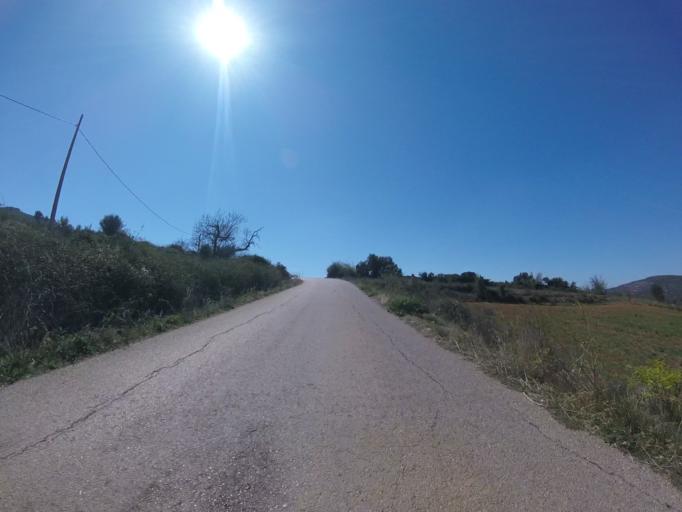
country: ES
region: Valencia
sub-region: Provincia de Castello
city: Chert/Xert
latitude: 40.4109
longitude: 0.1745
